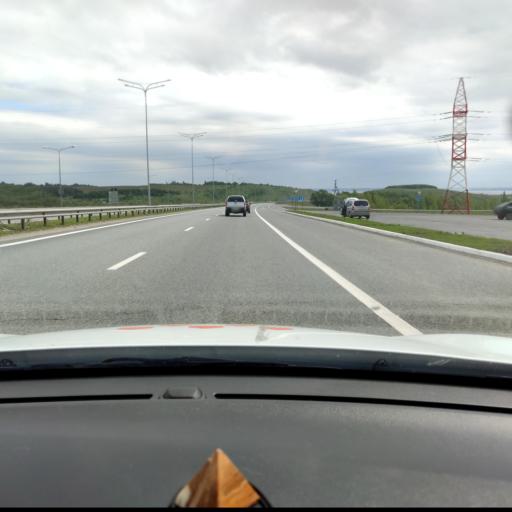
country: RU
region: Tatarstan
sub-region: Alekseyevskiy Rayon
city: Alekseyevskoye
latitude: 55.3815
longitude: 49.9532
